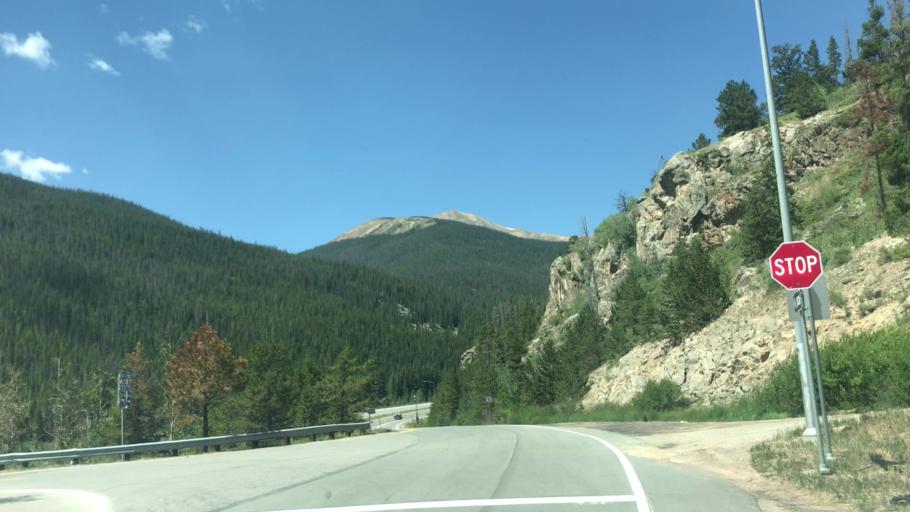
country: US
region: Colorado
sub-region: Clear Creek County
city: Georgetown
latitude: 39.6931
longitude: -105.8053
